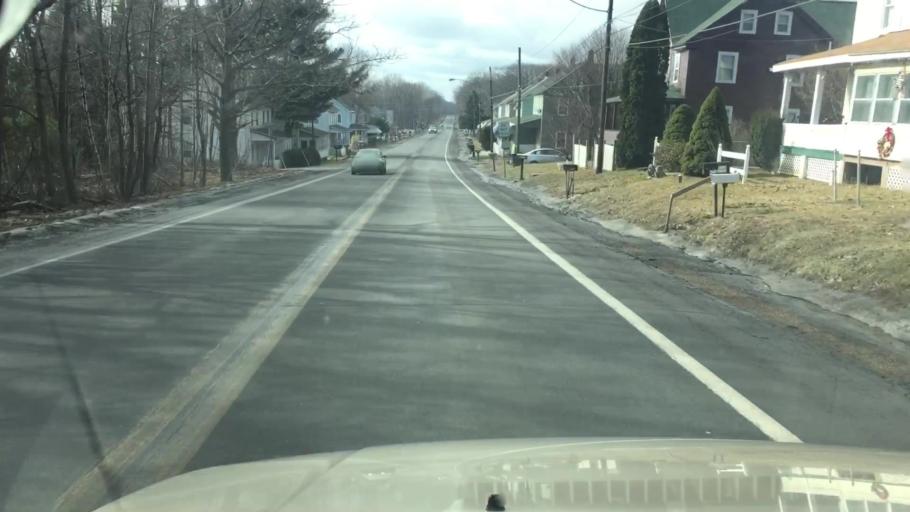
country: US
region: Pennsylvania
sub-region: Luzerne County
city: Oakdale
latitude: 40.9914
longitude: -75.9220
